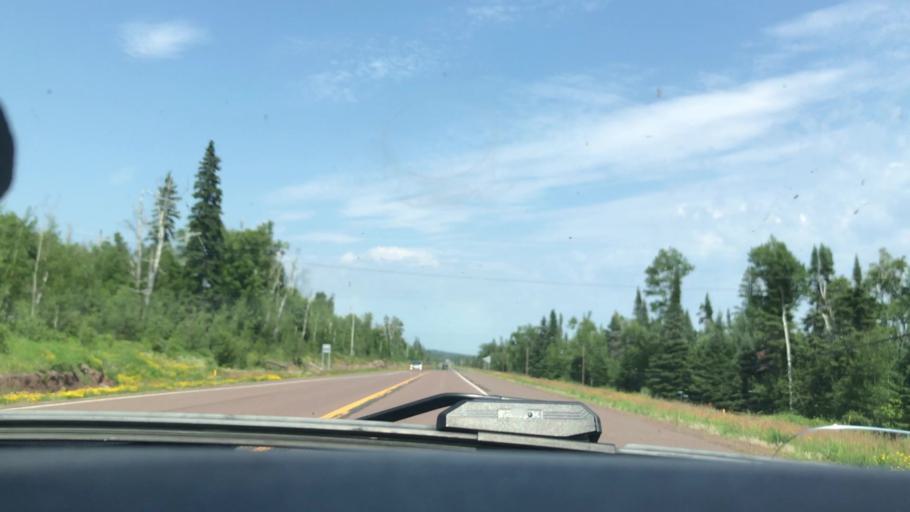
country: US
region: Minnesota
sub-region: Cook County
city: Grand Marais
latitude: 47.6203
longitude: -90.7494
